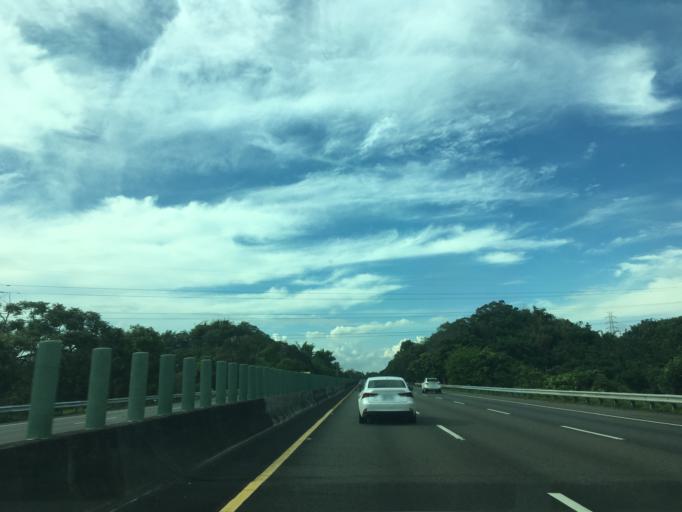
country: TW
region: Taiwan
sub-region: Chiayi
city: Jiayi Shi
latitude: 23.5595
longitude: 120.5050
